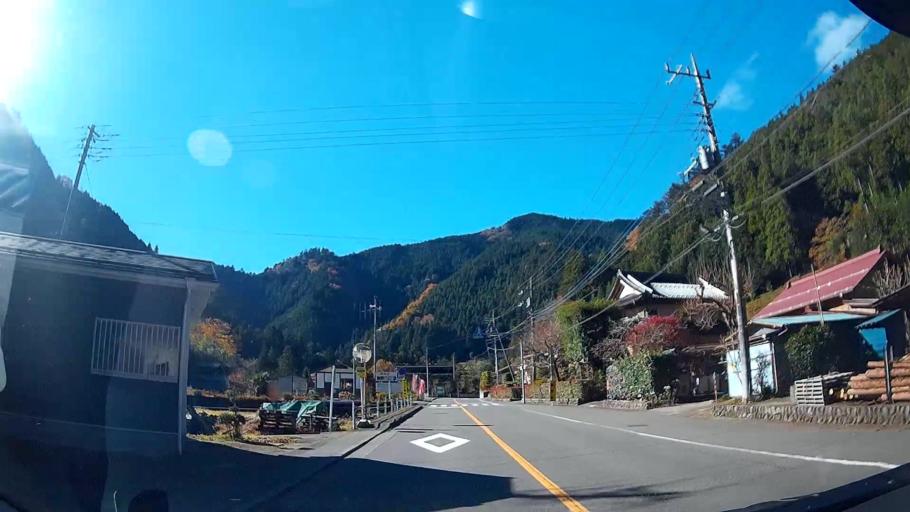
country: JP
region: Tokyo
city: Itsukaichi
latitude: 35.7154
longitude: 139.1513
